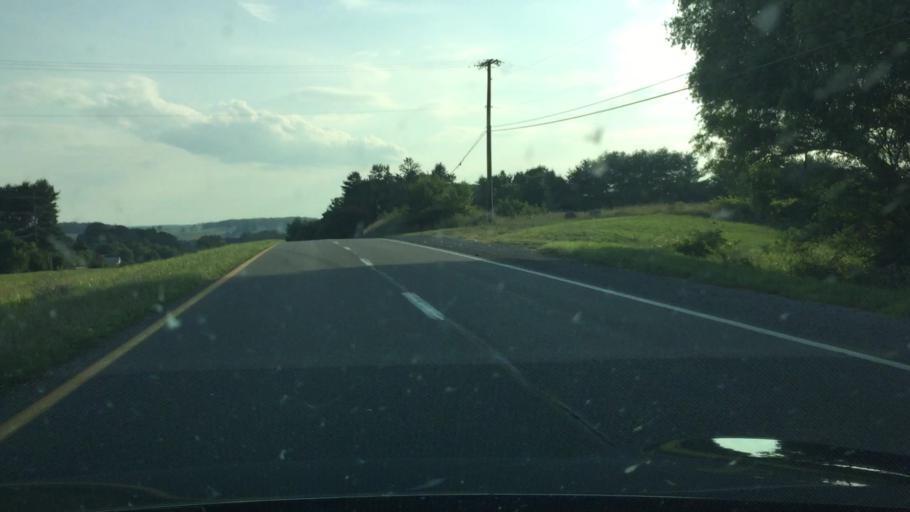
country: US
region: Virginia
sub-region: Pulaski County
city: Fairlawn
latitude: 37.1408
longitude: -80.6062
